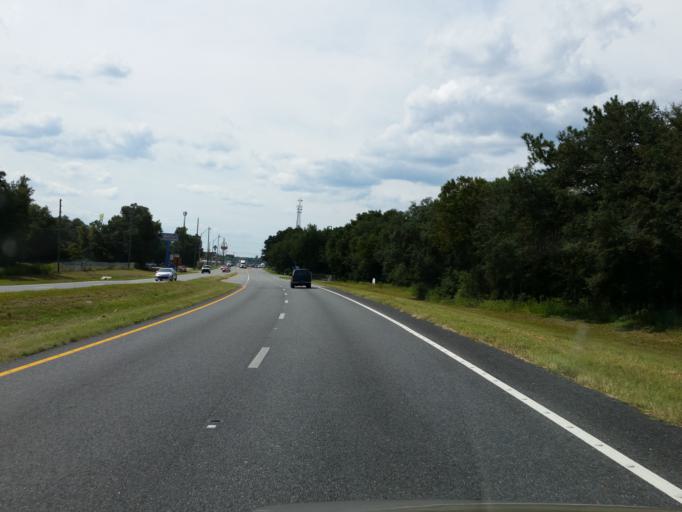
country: US
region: Florida
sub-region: Sumter County
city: Wildwood
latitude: 28.8713
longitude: -82.0847
